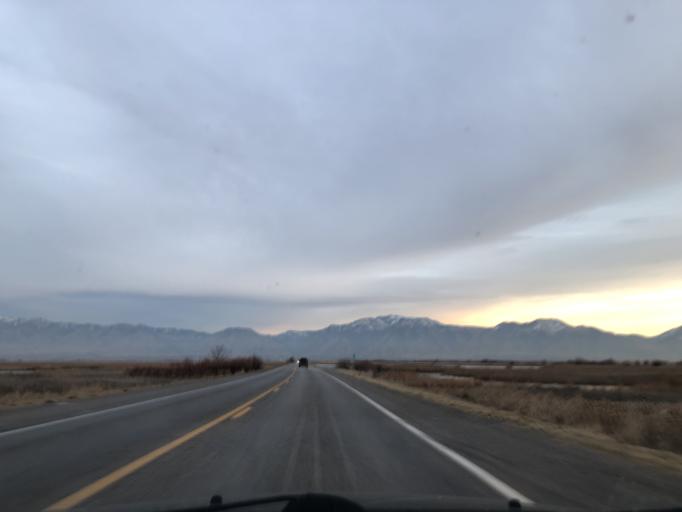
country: US
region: Utah
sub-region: Cache County
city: Benson
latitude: 41.7461
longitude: -111.9493
